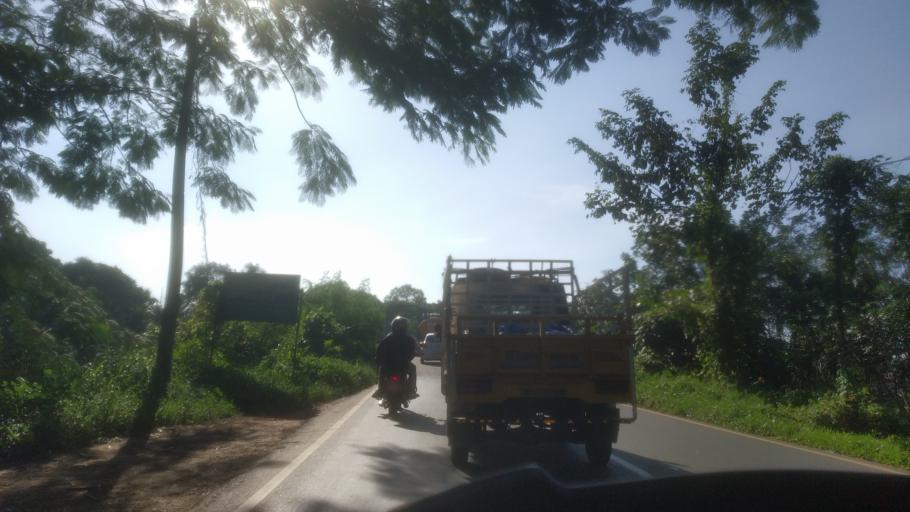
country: IN
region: Kerala
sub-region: Ernakulam
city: Ramamangalam
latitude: 9.9767
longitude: 76.5074
